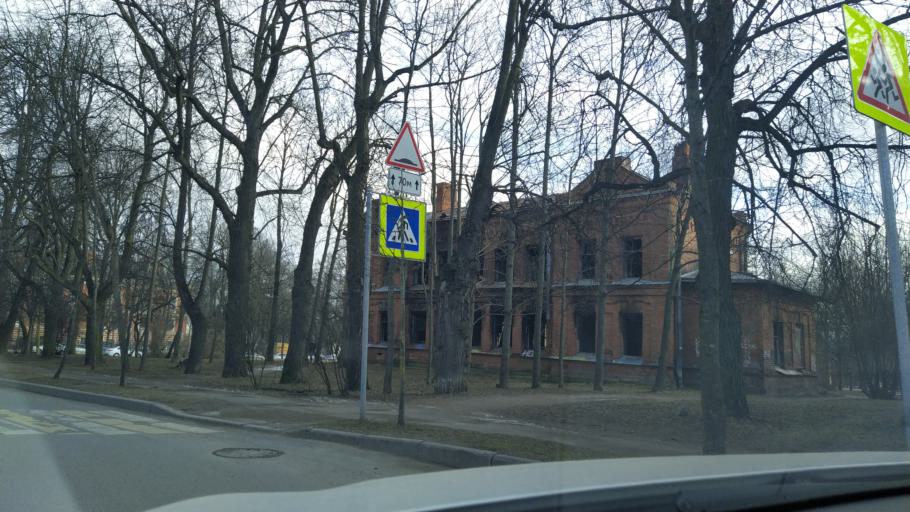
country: RU
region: St.-Petersburg
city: Pushkin
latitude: 59.7167
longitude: 30.4155
